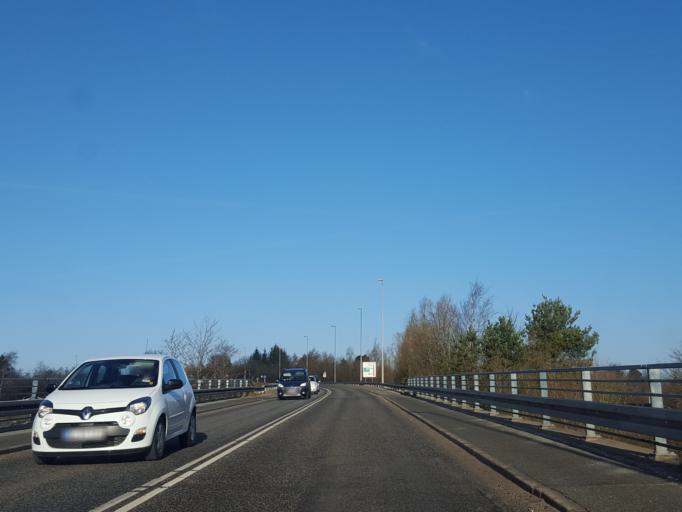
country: DK
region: North Denmark
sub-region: Alborg Kommune
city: Aalborg
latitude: 57.0120
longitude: 9.9060
